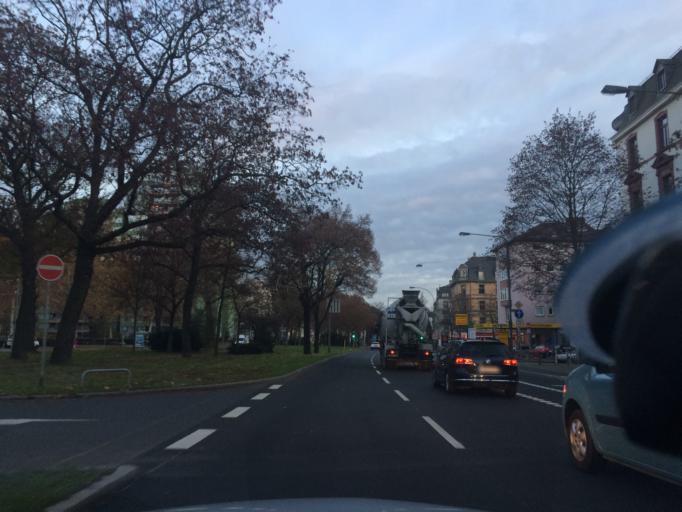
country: DE
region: Hesse
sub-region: Regierungsbezirk Darmstadt
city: Frankfurt am Main
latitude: 50.1272
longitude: 8.6962
